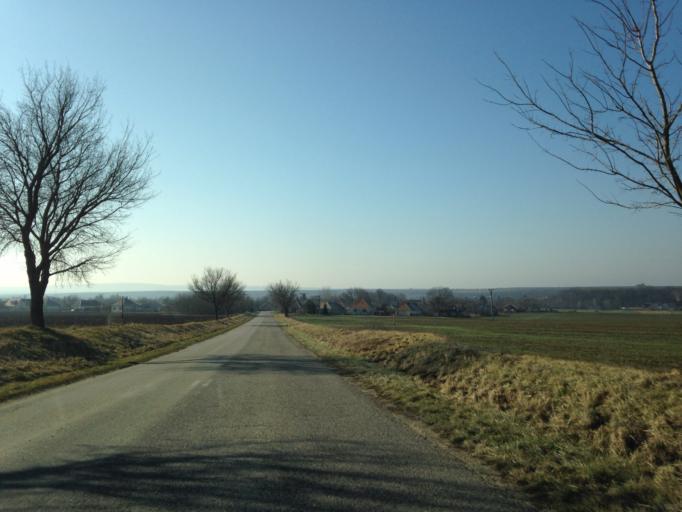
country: SK
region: Nitriansky
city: Svodin
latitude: 47.9368
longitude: 18.4075
